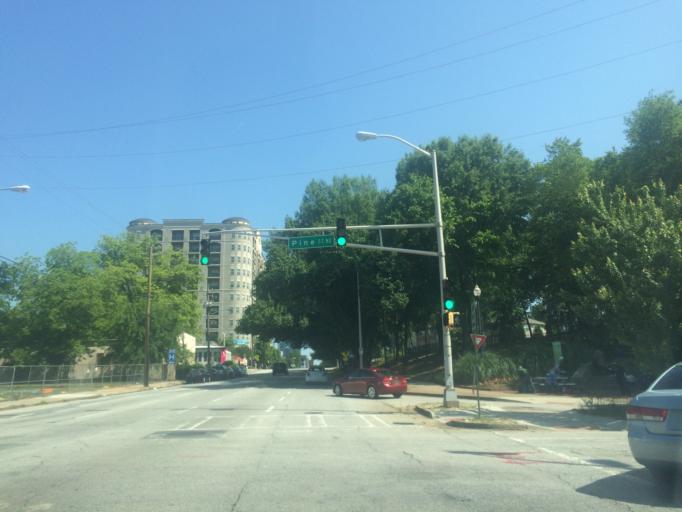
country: US
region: Georgia
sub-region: Fulton County
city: Atlanta
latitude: 33.7674
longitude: -84.3820
